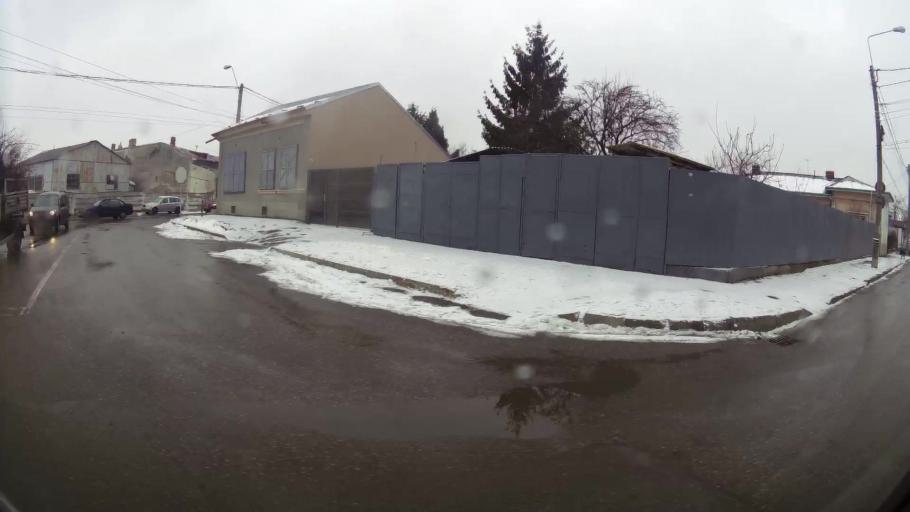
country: RO
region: Prahova
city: Ploiesti
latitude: 44.9531
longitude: 26.0220
